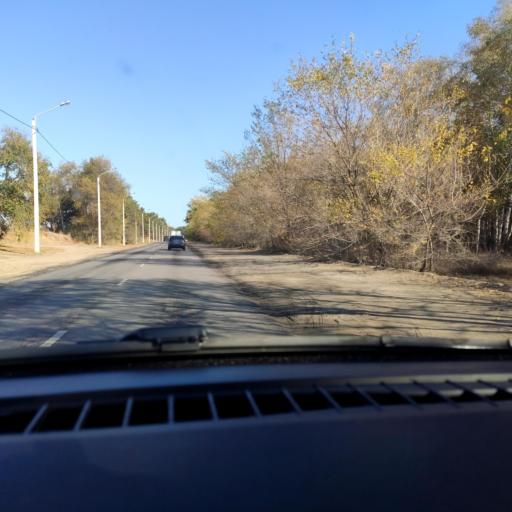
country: RU
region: Voronezj
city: Pridonskoy
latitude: 51.6915
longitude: 39.0831
